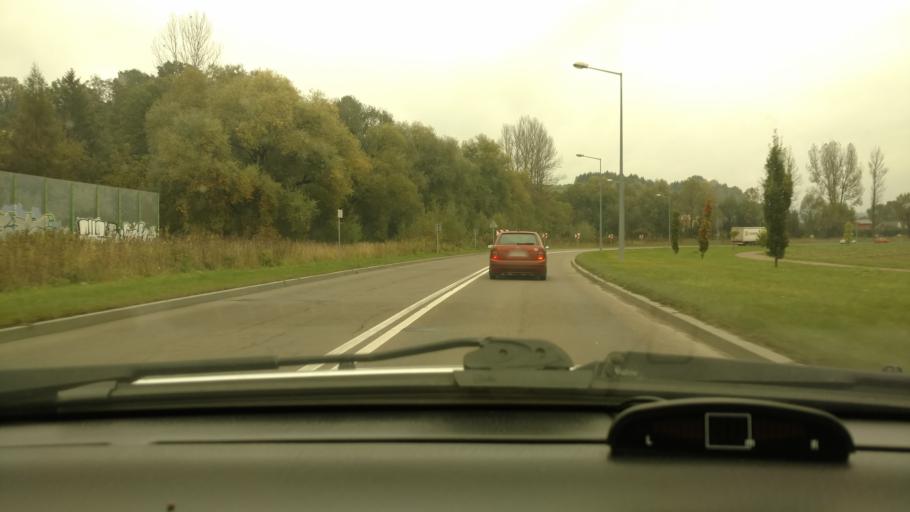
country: PL
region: Lesser Poland Voivodeship
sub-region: Powiat nowosadecki
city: Nowy Sacz
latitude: 49.6320
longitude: 20.7162
